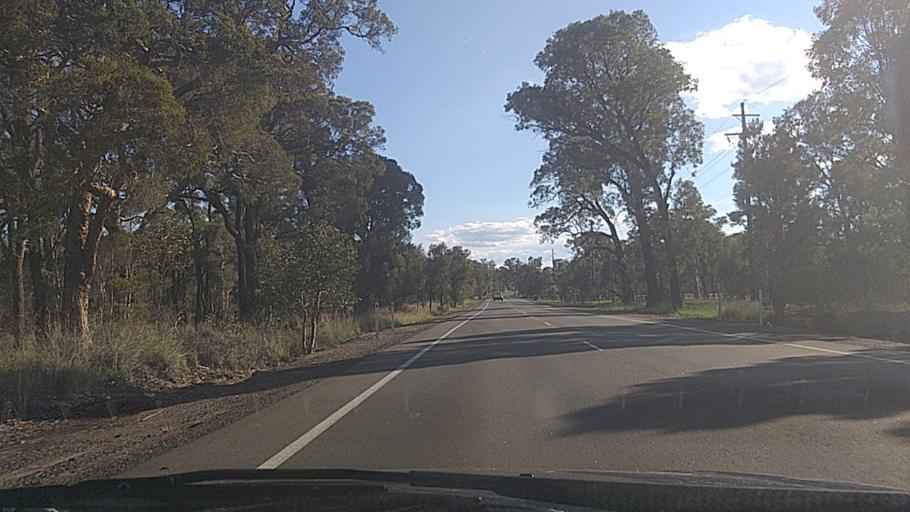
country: AU
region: New South Wales
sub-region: Penrith Municipality
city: Werrington Downs
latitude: -33.6801
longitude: 150.7422
